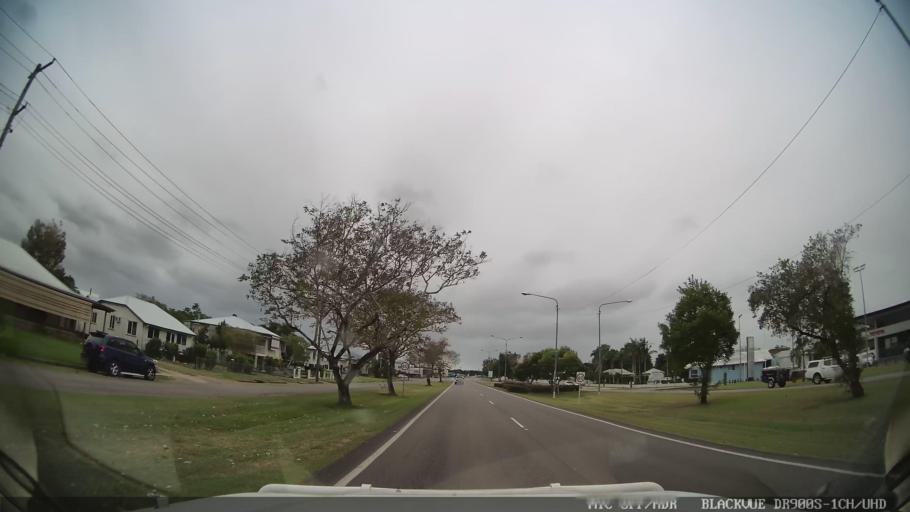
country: AU
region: Queensland
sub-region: Hinchinbrook
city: Ingham
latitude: -18.6447
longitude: 146.1624
